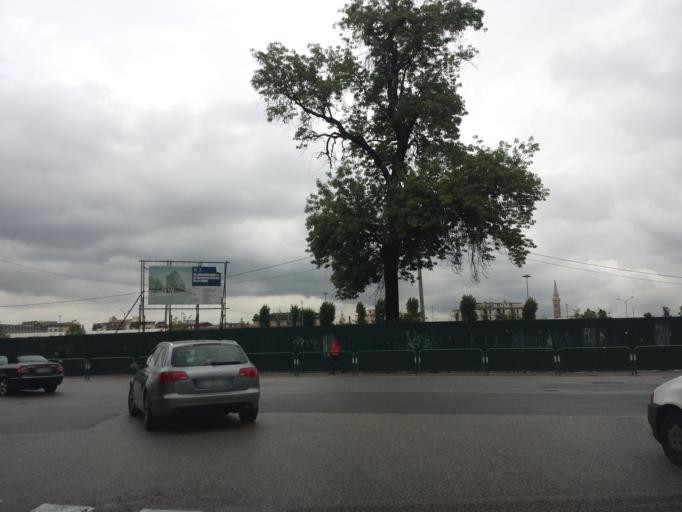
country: IT
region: Veneto
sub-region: Provincia di Padova
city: Padova
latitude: 45.4151
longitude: 11.8840
